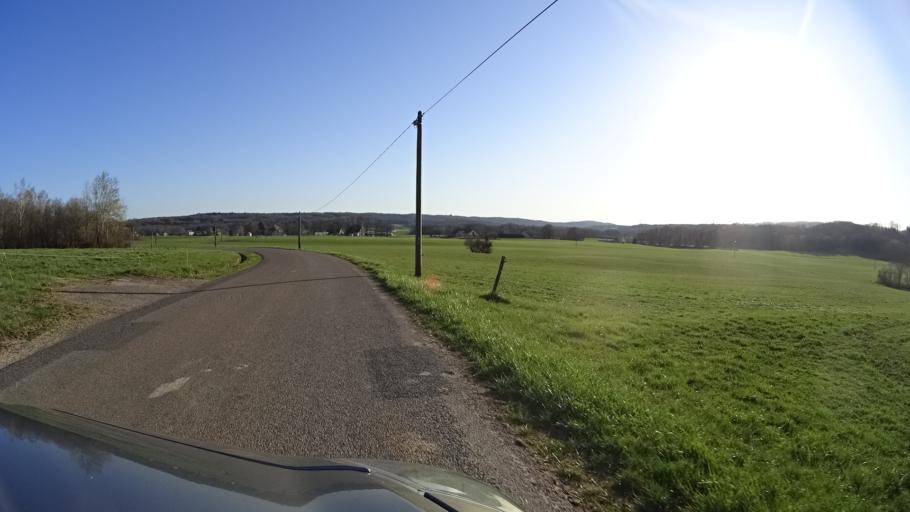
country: FR
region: Franche-Comte
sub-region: Departement du Doubs
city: Morre
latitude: 47.1939
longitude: 6.0497
